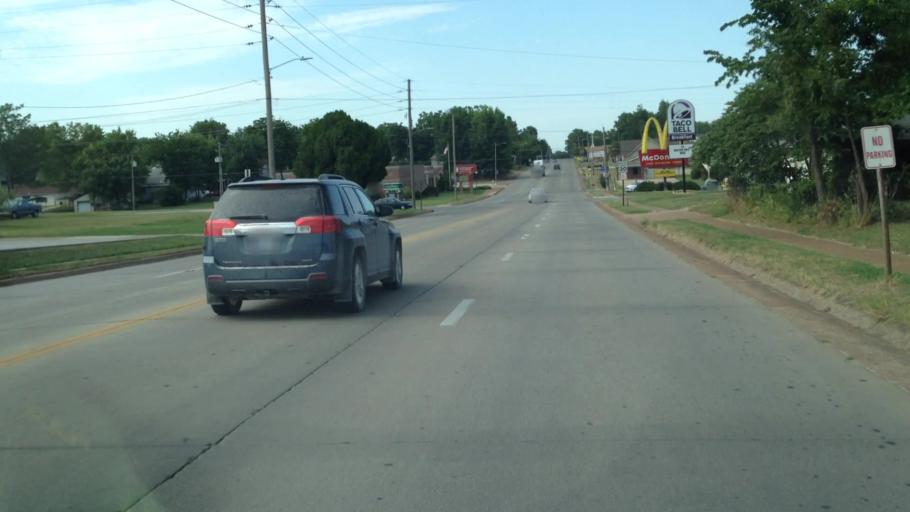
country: US
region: Kansas
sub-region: Labette County
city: Parsons
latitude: 37.3415
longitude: -95.2591
